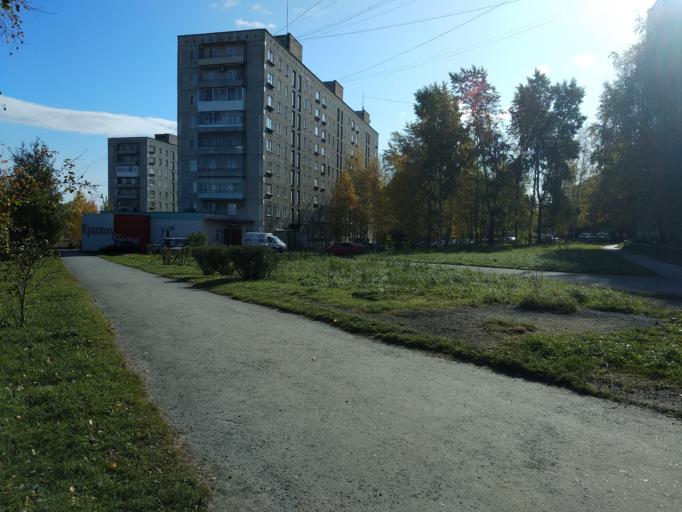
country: RU
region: Sverdlovsk
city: Krasnotur'insk
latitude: 59.7590
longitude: 60.1704
